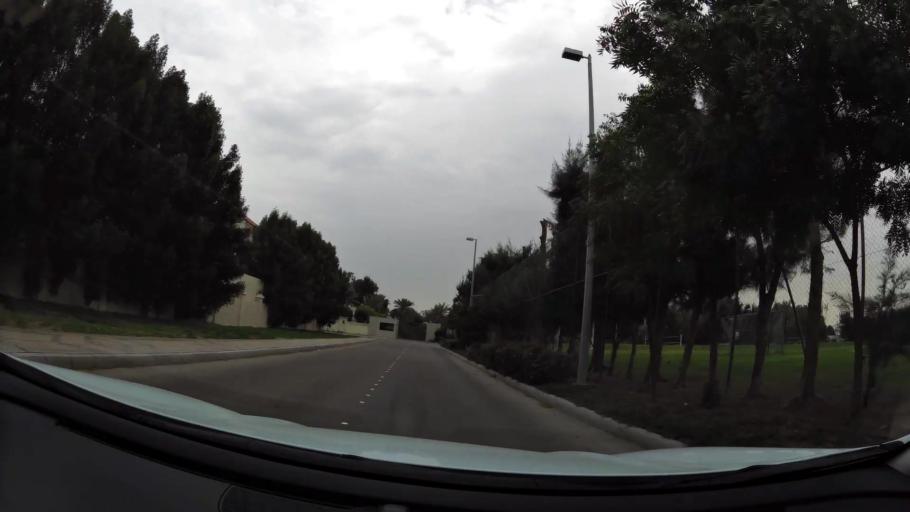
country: AE
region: Abu Dhabi
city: Abu Dhabi
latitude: 24.4420
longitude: 54.4421
